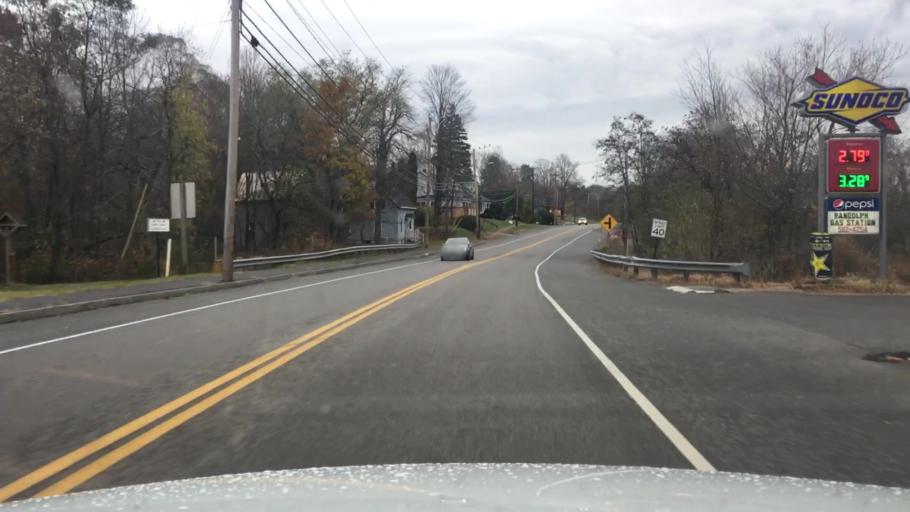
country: US
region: Maine
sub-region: Kennebec County
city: Randolph
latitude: 44.2285
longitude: -69.7646
